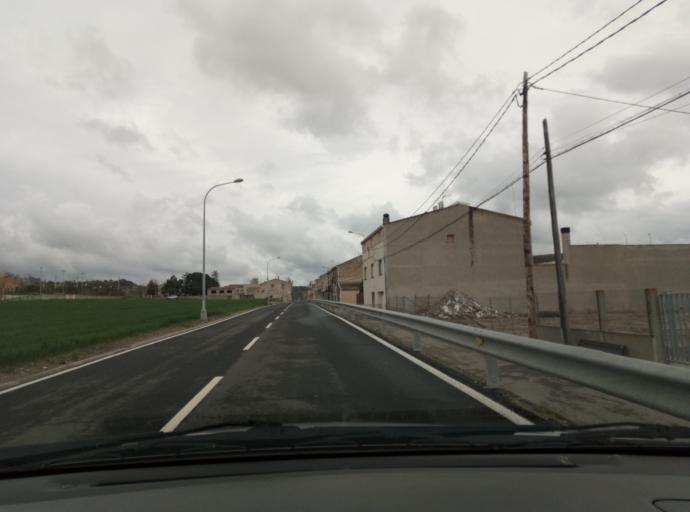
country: ES
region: Catalonia
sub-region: Provincia de Lleida
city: Cervera
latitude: 41.6309
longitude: 1.3391
